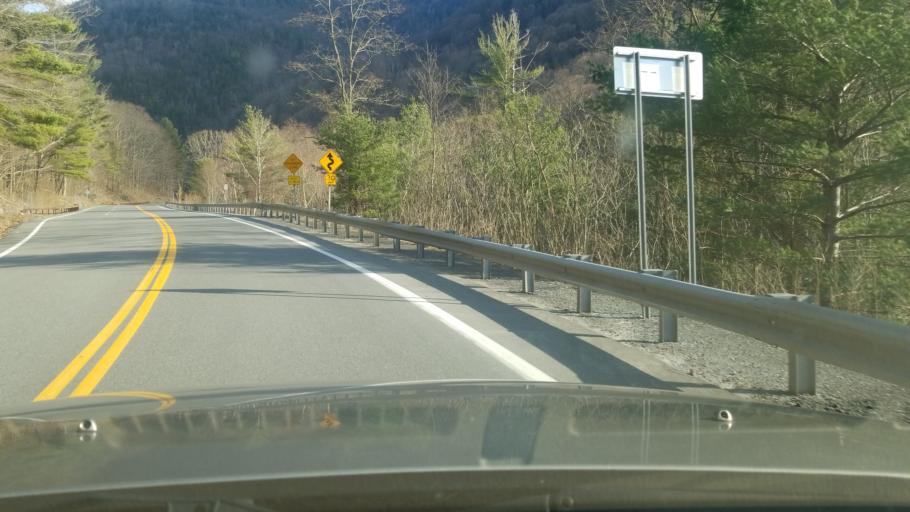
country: US
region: New York
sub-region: Greene County
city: Palenville
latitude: 42.1808
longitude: -74.0622
